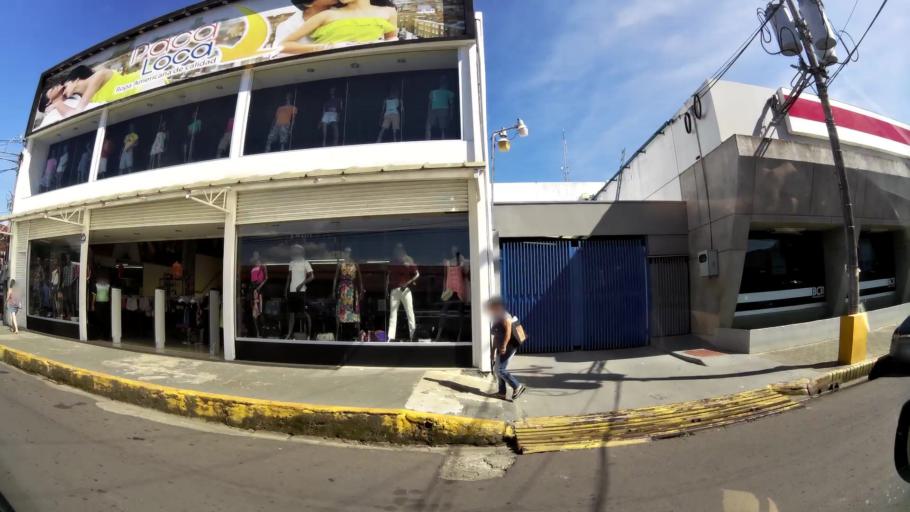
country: CR
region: San Jose
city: San Isidro
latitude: 9.3731
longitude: -83.7045
